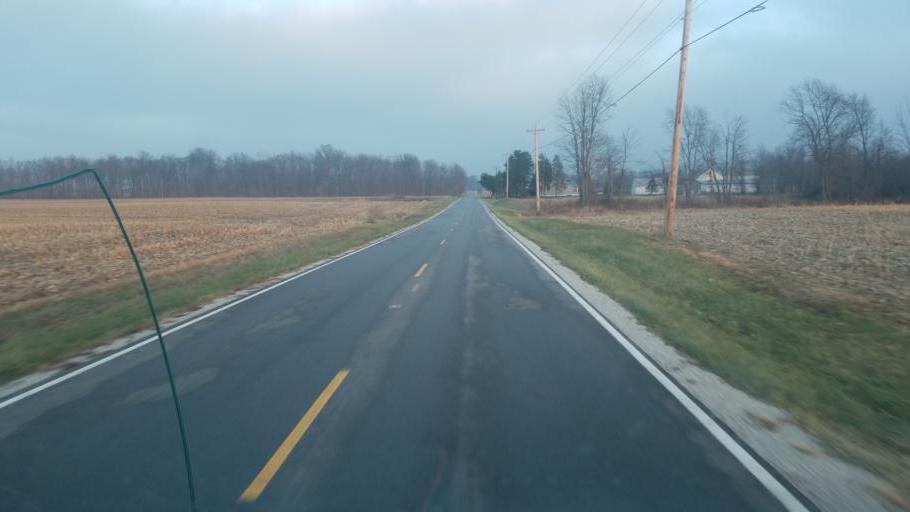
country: US
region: Ohio
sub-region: Wyandot County
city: Carey
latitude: 40.9998
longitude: -83.2858
